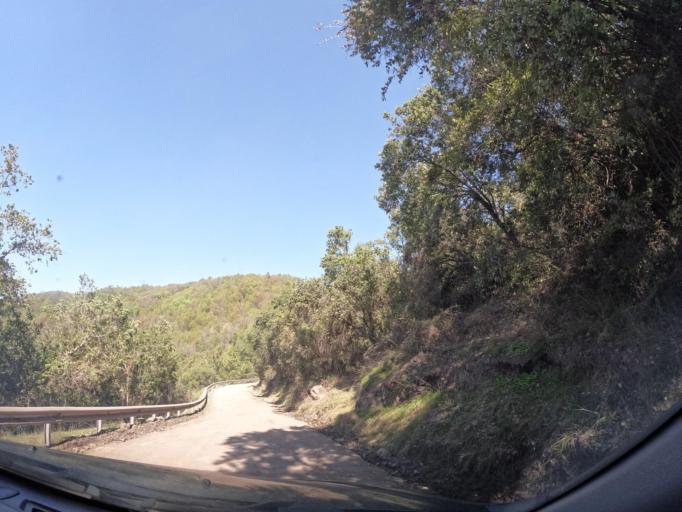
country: CL
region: Maule
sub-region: Provincia de Linares
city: Longavi
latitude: -36.2419
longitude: -71.4410
